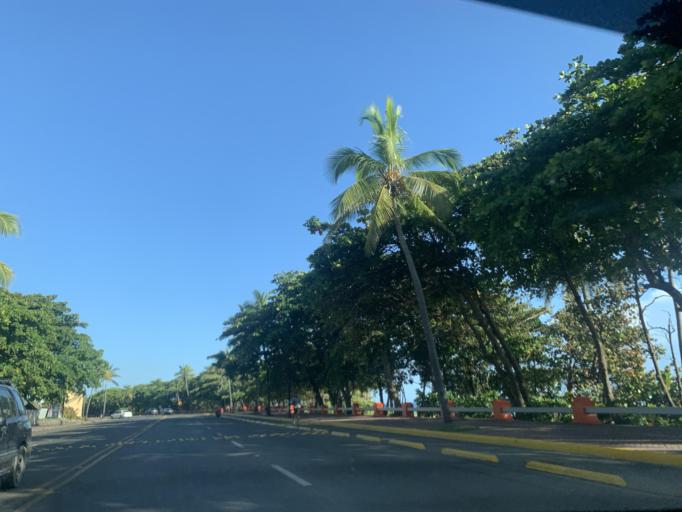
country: DO
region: Puerto Plata
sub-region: Puerto Plata
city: Puerto Plata
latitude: 19.7922
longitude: -70.6754
